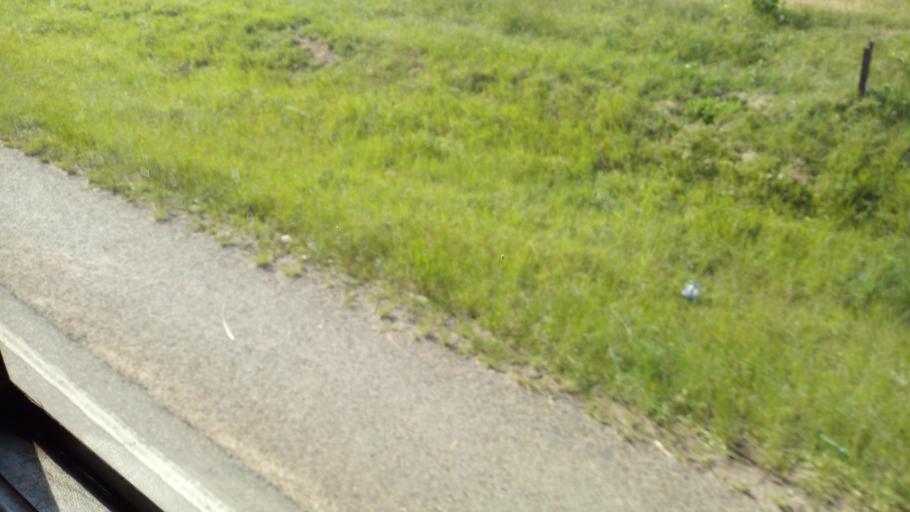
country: UG
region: Central Region
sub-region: Lyantonde District
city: Lyantonde
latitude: -0.4610
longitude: 31.0402
